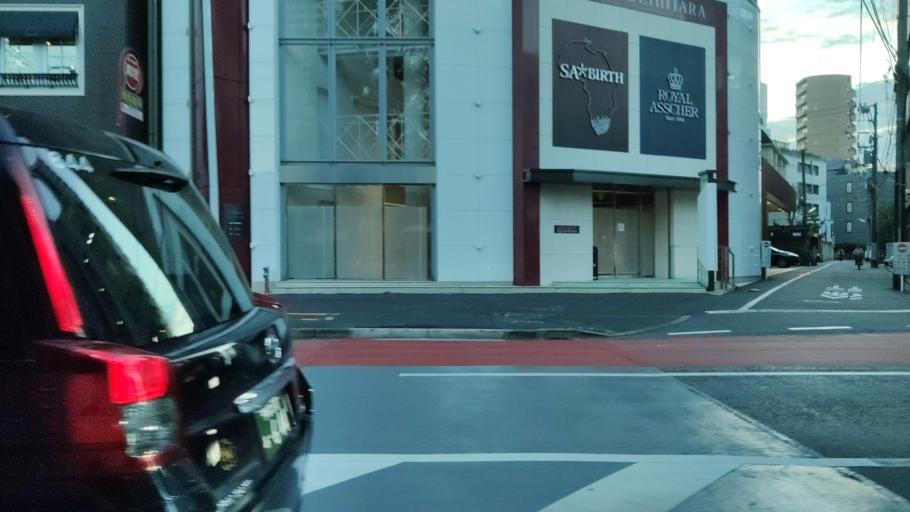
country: JP
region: Tokyo
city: Tokyo
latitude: 35.6668
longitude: 139.7275
